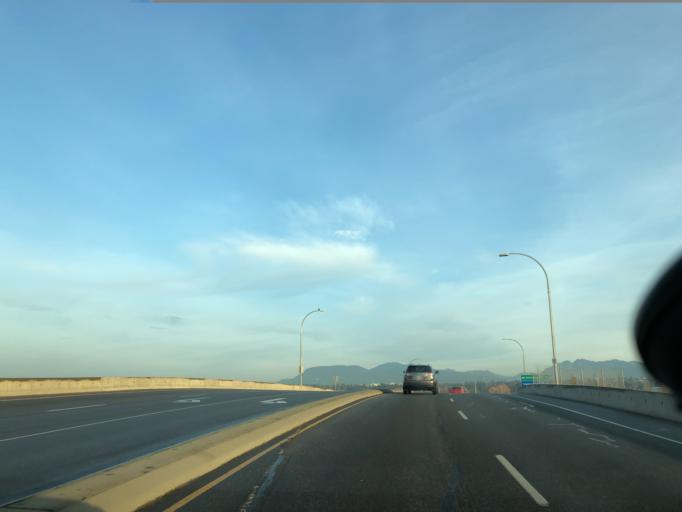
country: CA
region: British Columbia
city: Richmond
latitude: 49.1942
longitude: -123.1508
